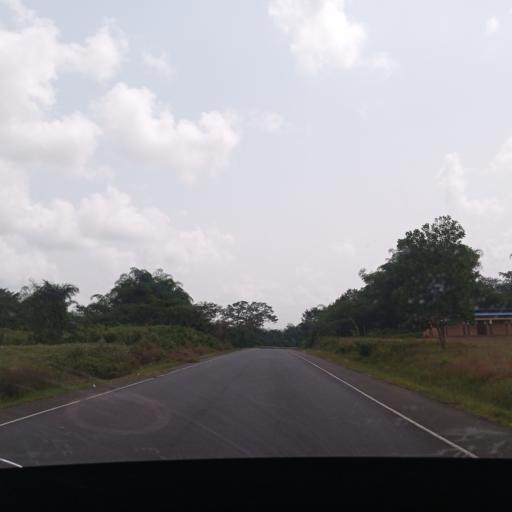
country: LR
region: Margibi
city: Kakata
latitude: 6.2429
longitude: -10.2884
